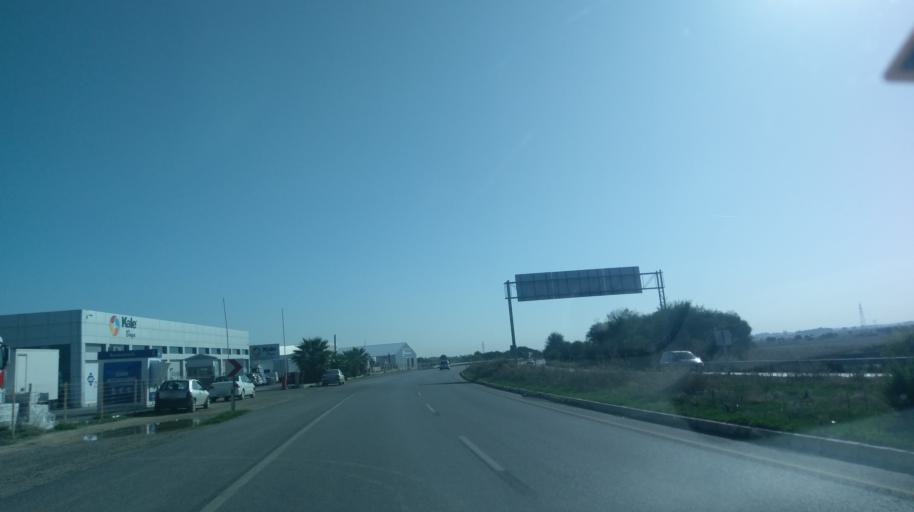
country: CY
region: Ammochostos
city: Lefkonoiko
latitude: 35.2077
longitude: 33.5935
